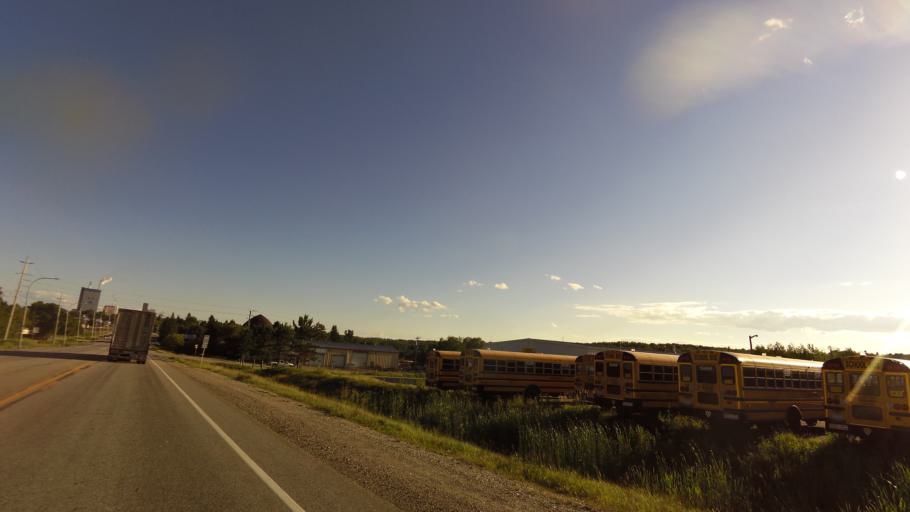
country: CA
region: Ontario
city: Dryden
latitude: 49.7980
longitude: -92.8474
